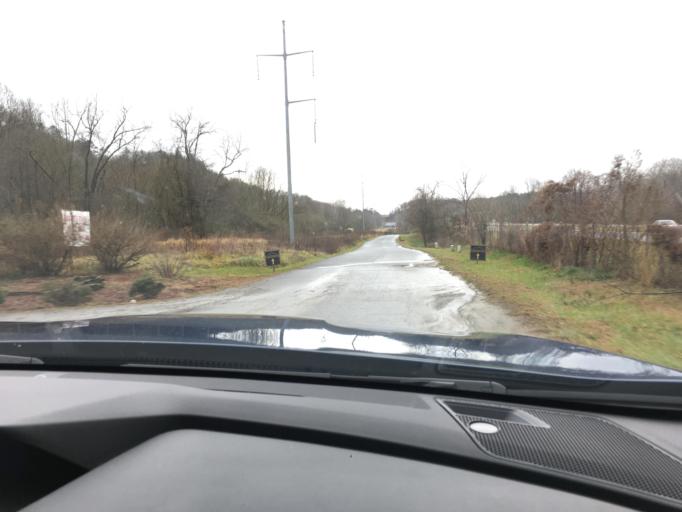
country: US
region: North Carolina
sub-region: Cherokee County
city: Andrews
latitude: 35.1637
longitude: -83.9370
